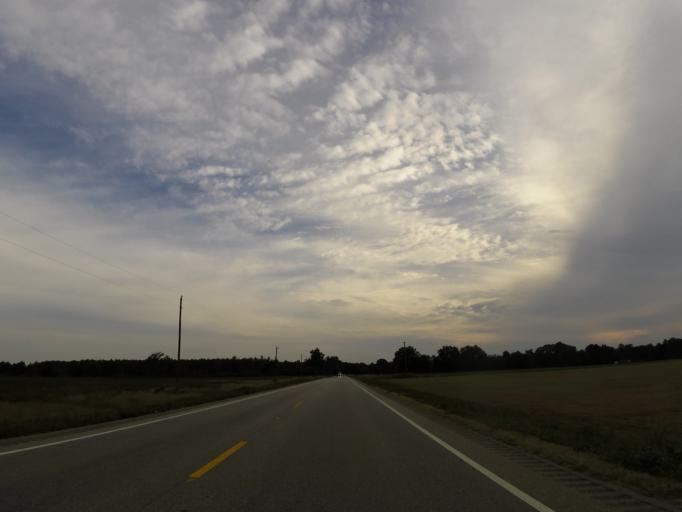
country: US
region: Alabama
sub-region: Monroe County
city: Frisco City
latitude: 31.3682
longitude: -87.4317
